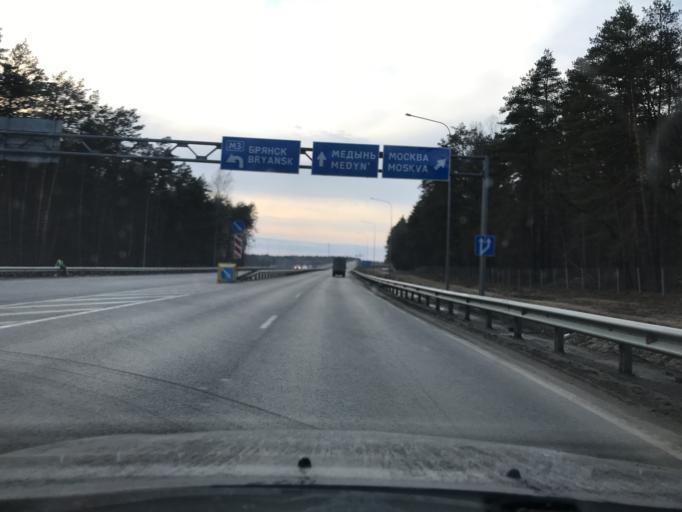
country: RU
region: Kaluga
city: Mstikhino
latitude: 54.5818
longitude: 36.0848
